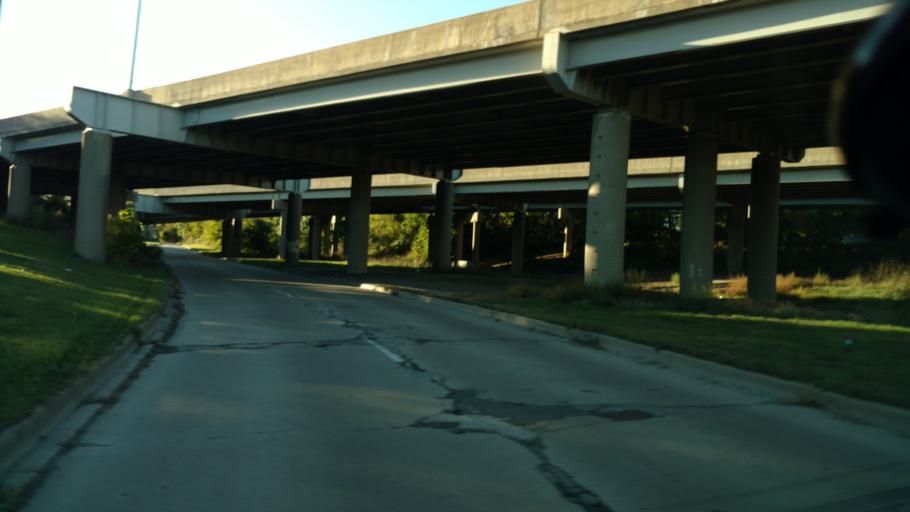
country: US
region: Michigan
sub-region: Ingham County
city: Lansing
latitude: 42.7262
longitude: -84.5335
